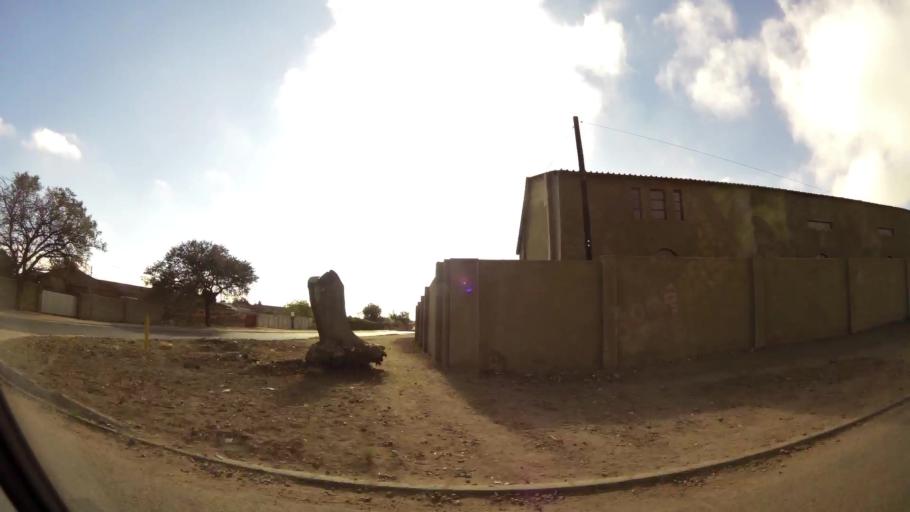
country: ZA
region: Limpopo
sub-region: Capricorn District Municipality
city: Polokwane
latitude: -23.8486
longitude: 29.3805
